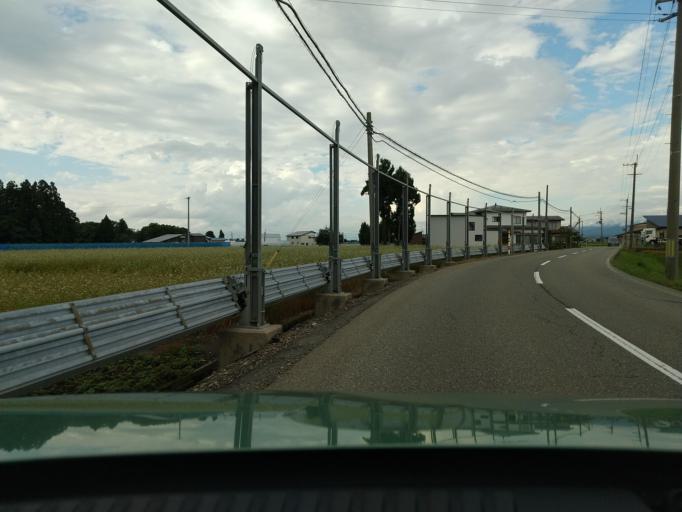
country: JP
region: Akita
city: Yokotemachi
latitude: 39.2932
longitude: 140.4828
